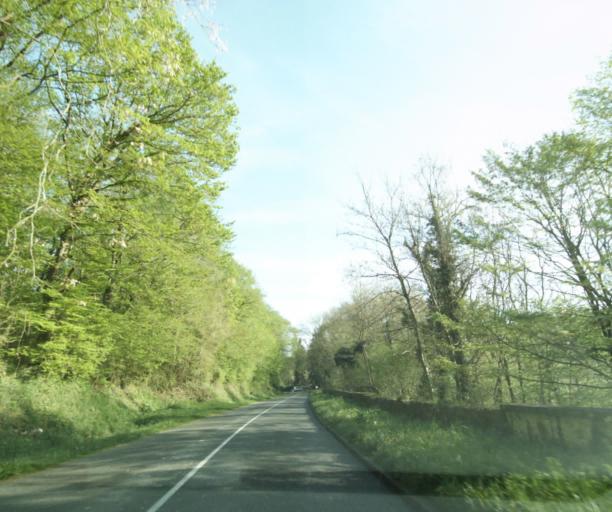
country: FR
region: Ile-de-France
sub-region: Departement de Seine-et-Marne
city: Vernou-la-Celle-sur-Seine
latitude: 48.4537
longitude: 2.8594
